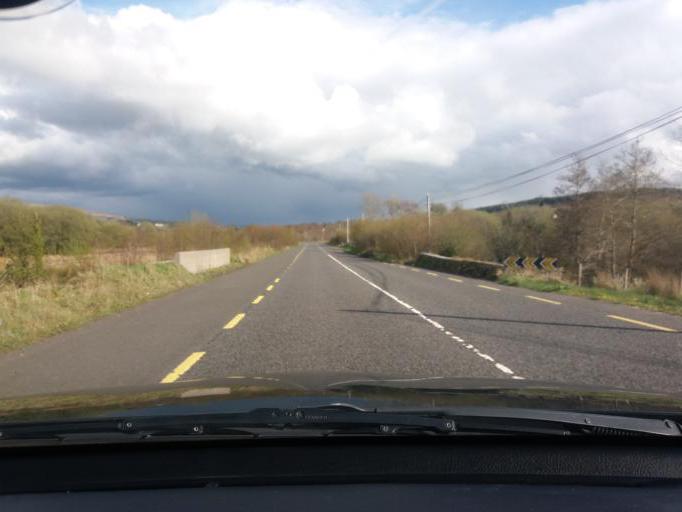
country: IE
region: Connaught
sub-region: County Leitrim
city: Manorhamilton
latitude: 54.3512
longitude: -8.2473
